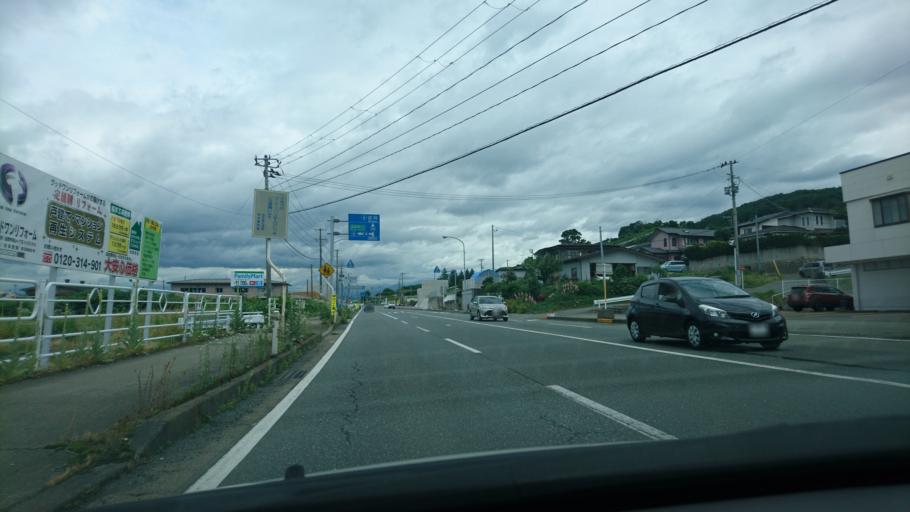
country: JP
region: Iwate
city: Morioka-shi
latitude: 39.6586
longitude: 141.1804
